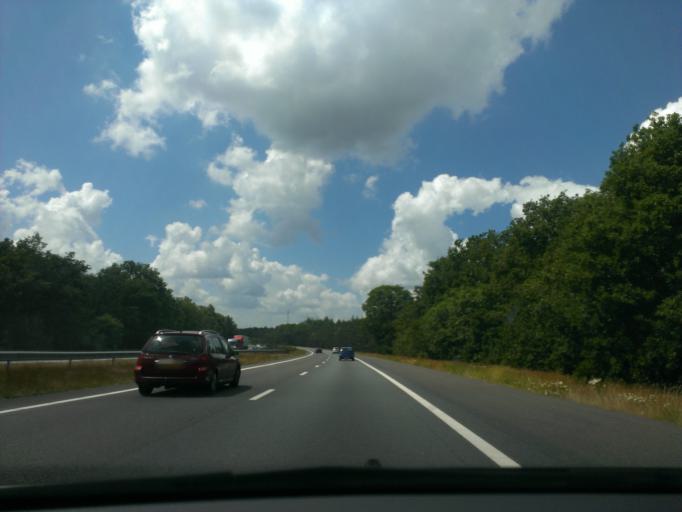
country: NL
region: Gelderland
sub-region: Gemeente Apeldoorn
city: Uddel
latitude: 52.2030
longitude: 5.8213
